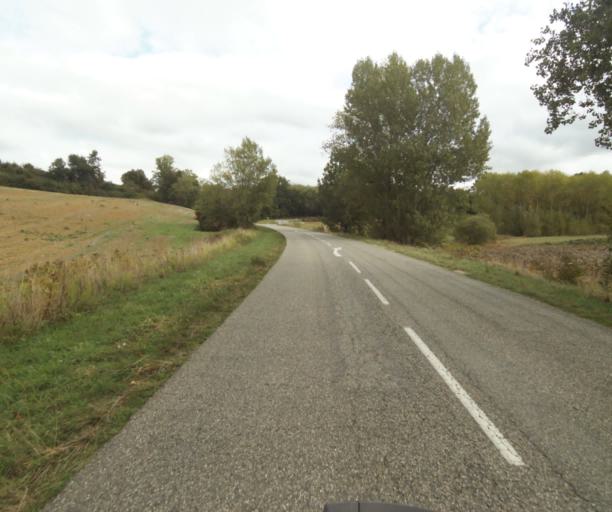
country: FR
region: Midi-Pyrenees
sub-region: Departement du Tarn-et-Garonne
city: Finhan
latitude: 43.8579
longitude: 1.1097
